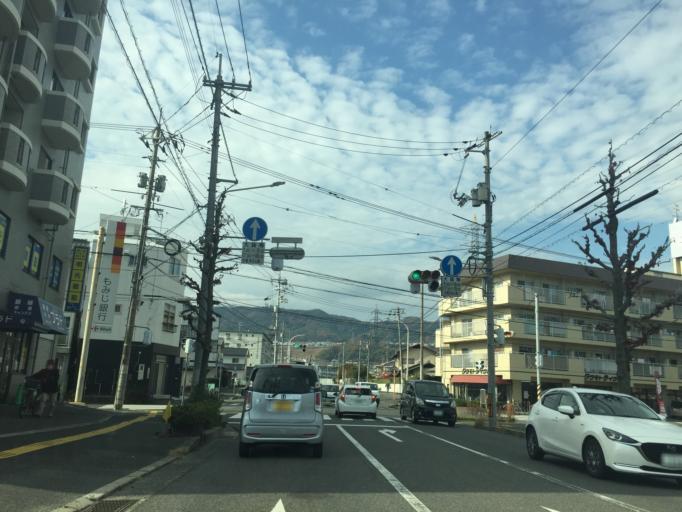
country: JP
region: Hiroshima
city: Hiroshima-shi
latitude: 34.4342
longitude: 132.4606
